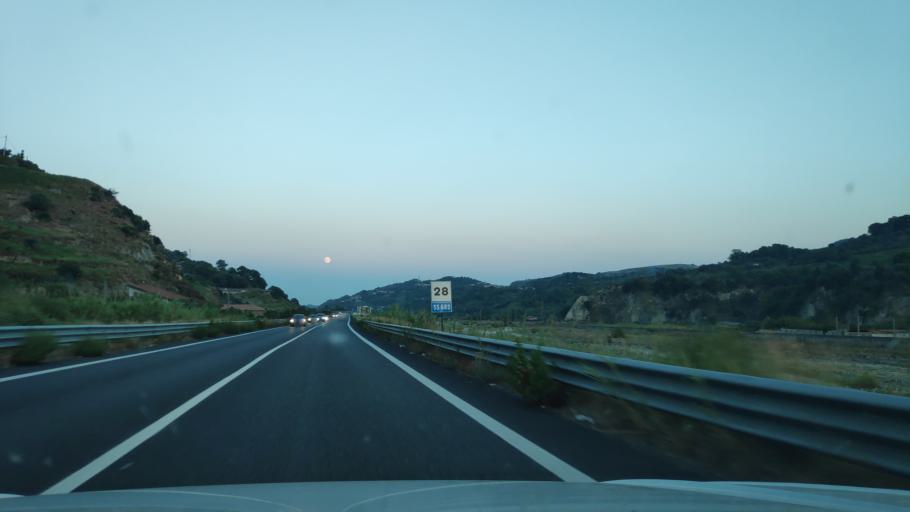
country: IT
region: Calabria
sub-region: Provincia di Reggio Calabria
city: Mammola
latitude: 38.3551
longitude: 16.2420
